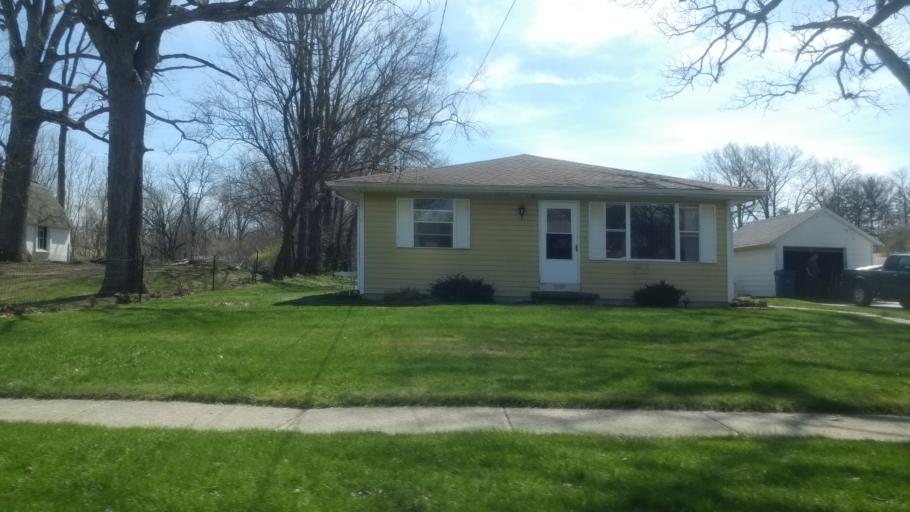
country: US
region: Ohio
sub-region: Wood County
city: Bowling Green
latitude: 41.3787
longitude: -83.6584
